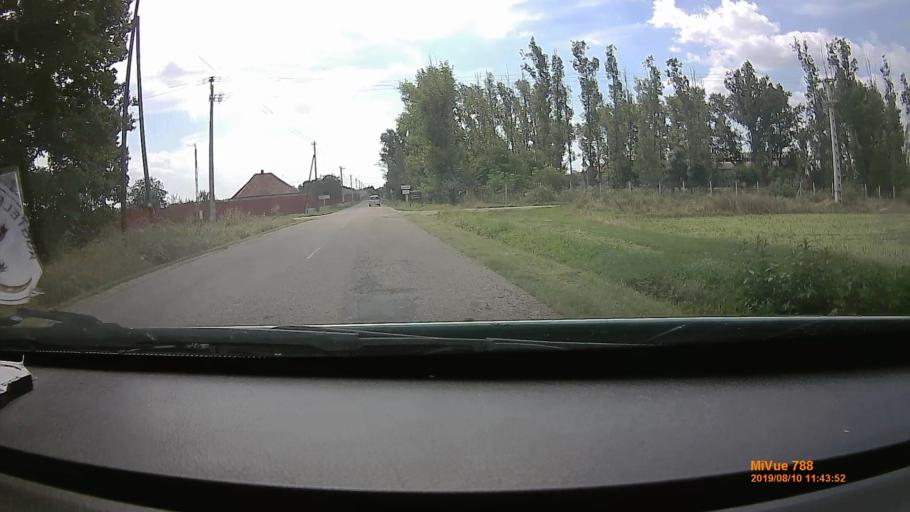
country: HU
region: Borsod-Abauj-Zemplen
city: Szentistvan
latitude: 47.7254
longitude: 20.6197
